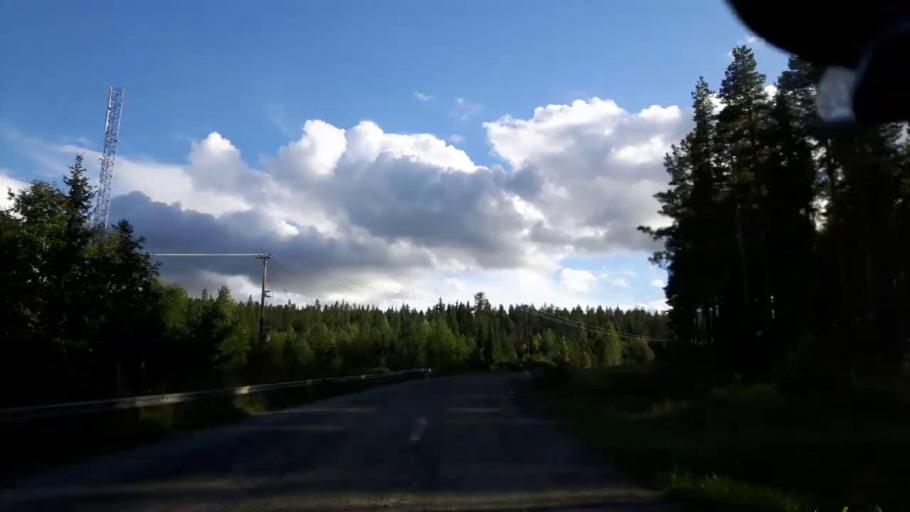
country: SE
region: Jaemtland
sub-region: Stroemsunds Kommun
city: Stroemsund
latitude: 63.3468
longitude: 15.5722
